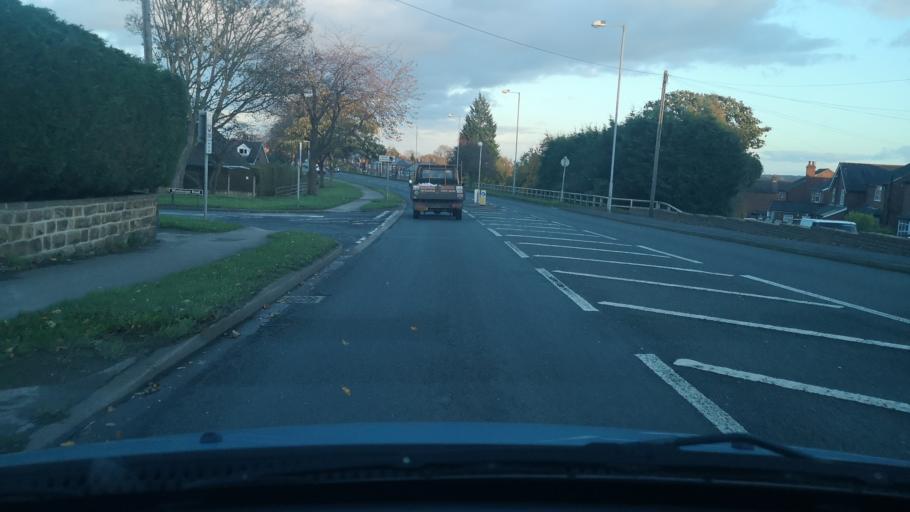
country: GB
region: England
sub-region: City and Borough of Wakefield
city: Horbury
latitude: 53.6567
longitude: -1.5534
